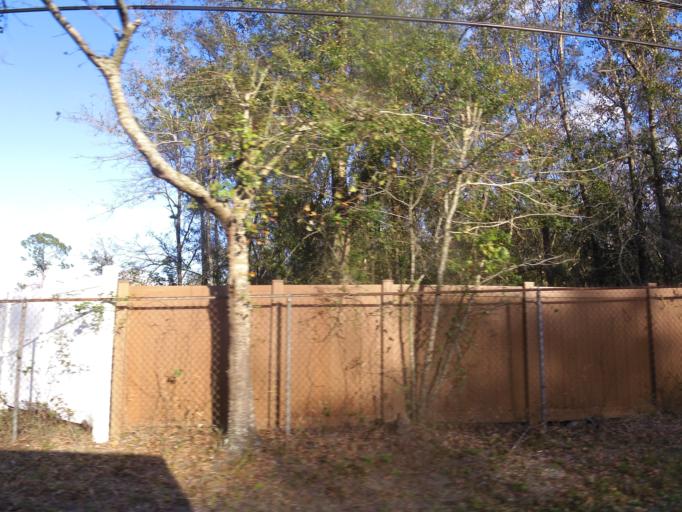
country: US
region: Florida
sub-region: Duval County
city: Jacksonville
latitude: 30.2679
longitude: -81.5741
